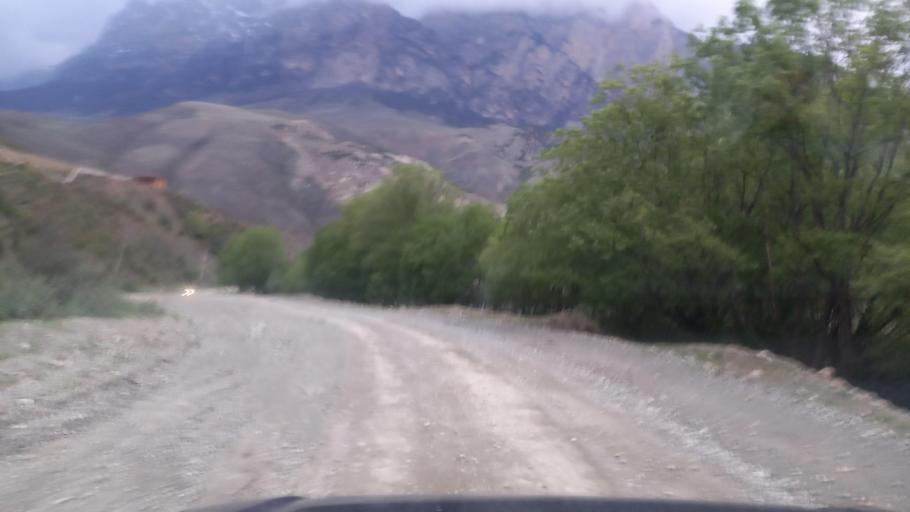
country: RU
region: North Ossetia
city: Mizur
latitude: 42.8552
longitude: 44.1515
